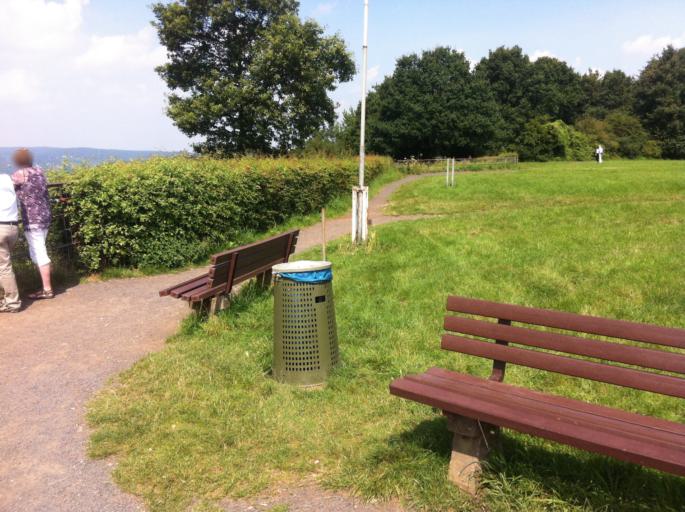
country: DE
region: Rheinland-Pfalz
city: Erpel
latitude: 50.5823
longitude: 7.2458
